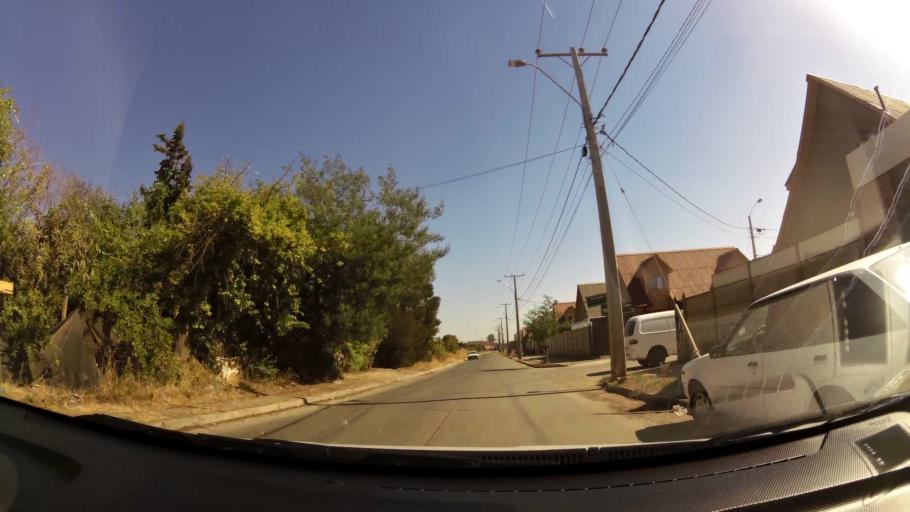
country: CL
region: Maule
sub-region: Provincia de Talca
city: Talca
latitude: -35.4084
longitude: -71.6180
